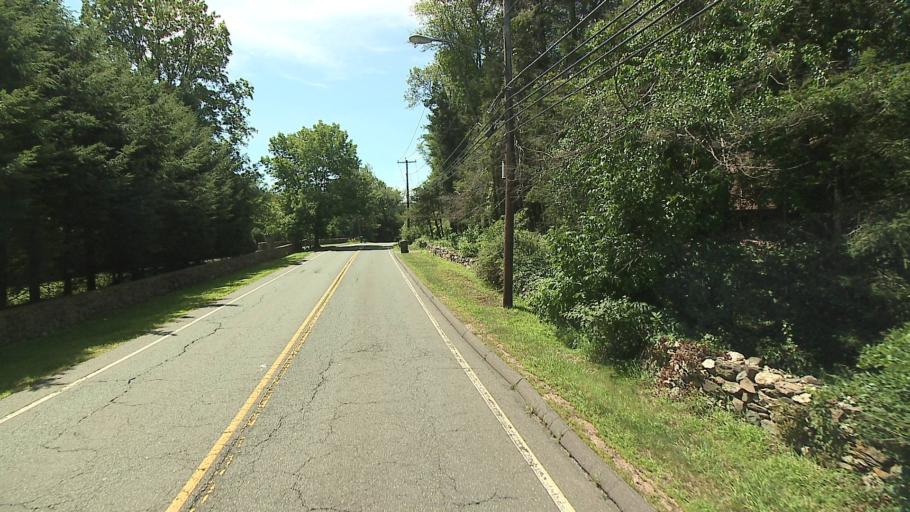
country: US
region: Connecticut
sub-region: Hartford County
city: Canton Valley
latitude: 41.8716
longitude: -72.8989
